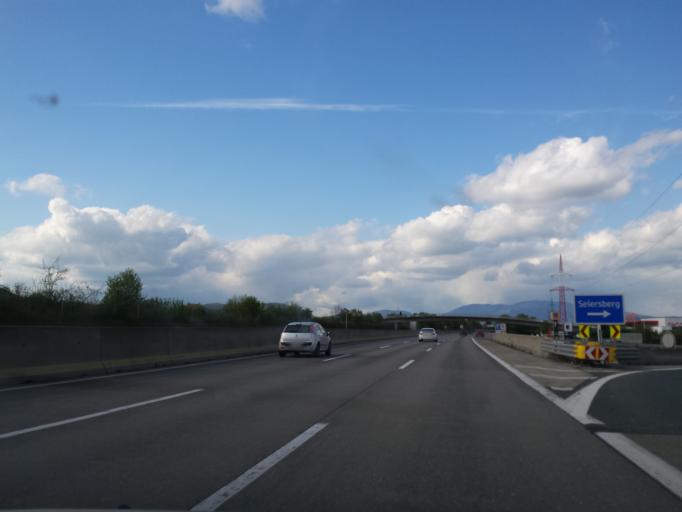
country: AT
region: Styria
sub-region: Politischer Bezirk Graz-Umgebung
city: Seiersberg
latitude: 47.0121
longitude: 15.4077
